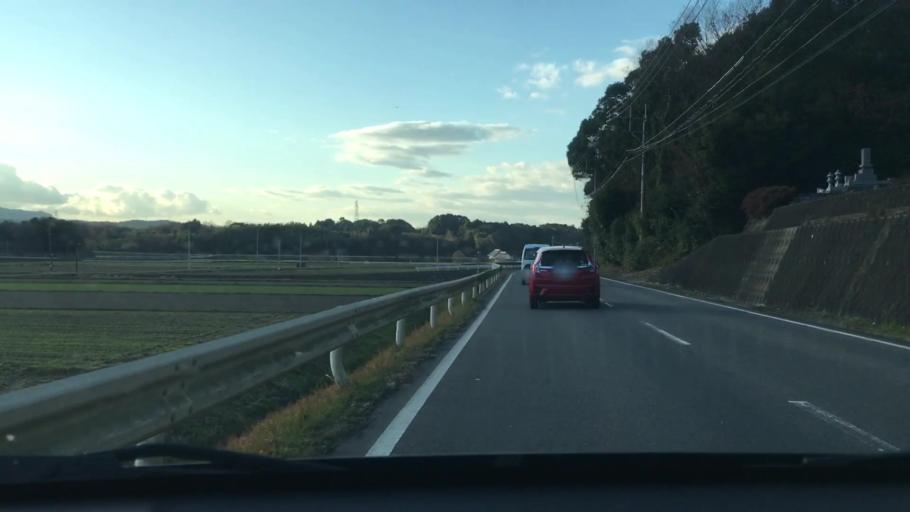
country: JP
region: Oita
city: Bungo-Takada-shi
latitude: 33.5106
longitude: 131.3571
